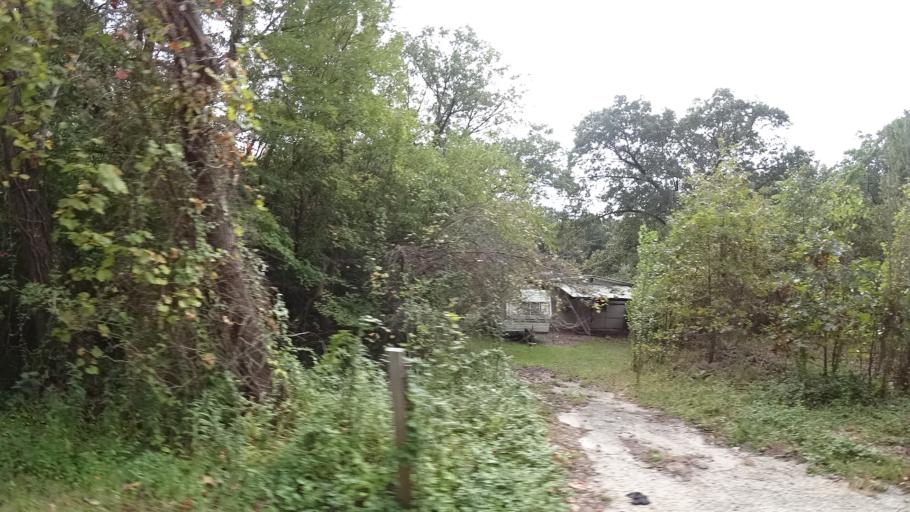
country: US
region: Indiana
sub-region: LaPorte County
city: Long Beach
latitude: 41.7386
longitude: -86.8379
